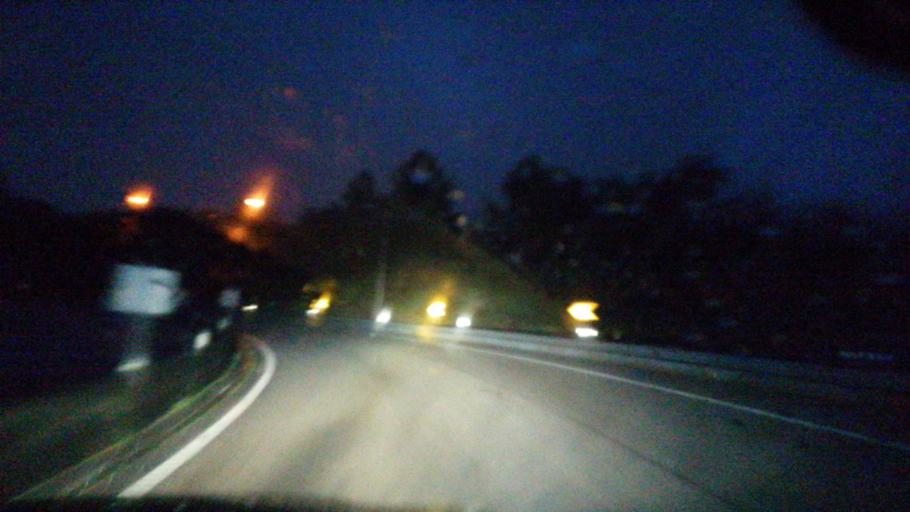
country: PT
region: Braga
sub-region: Vizela
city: Vizela
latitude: 41.4040
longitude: -8.2526
